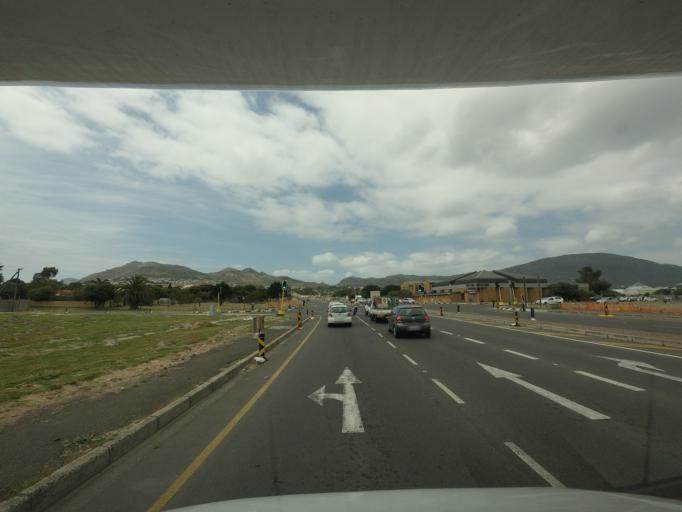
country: ZA
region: Western Cape
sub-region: City of Cape Town
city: Constantia
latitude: -34.1211
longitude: 18.3915
